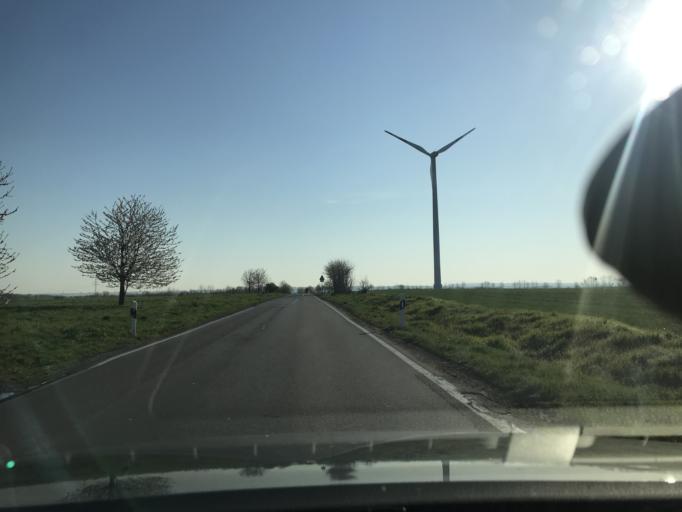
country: DE
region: Saxony-Anhalt
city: Holleben
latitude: 51.4278
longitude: 11.8734
